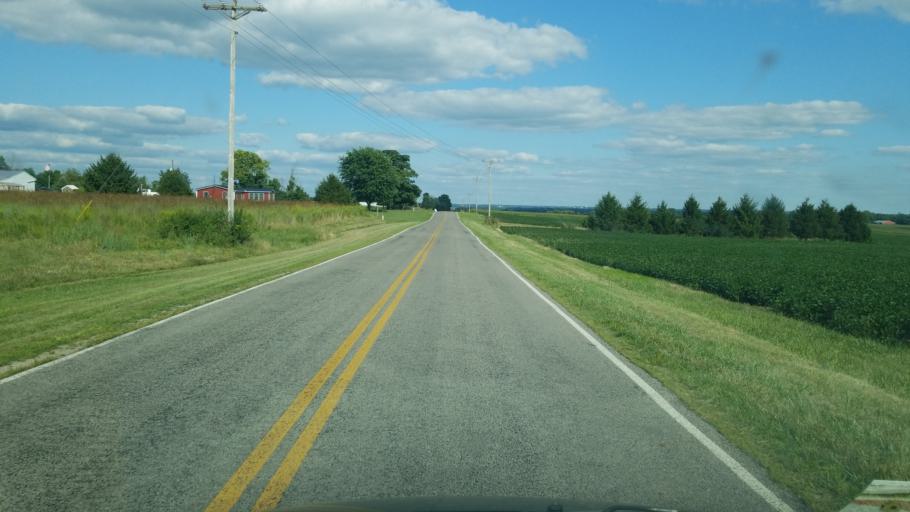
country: US
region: Ohio
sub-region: Champaign County
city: Saint Paris
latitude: 40.1333
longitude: -83.8680
